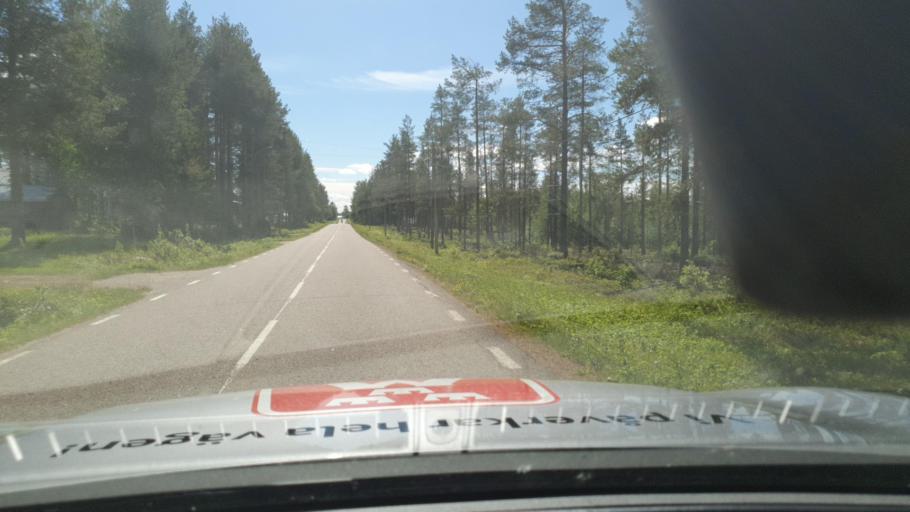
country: SE
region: Norrbotten
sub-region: Overkalix Kommun
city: OEverkalix
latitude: 67.0086
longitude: 22.4848
